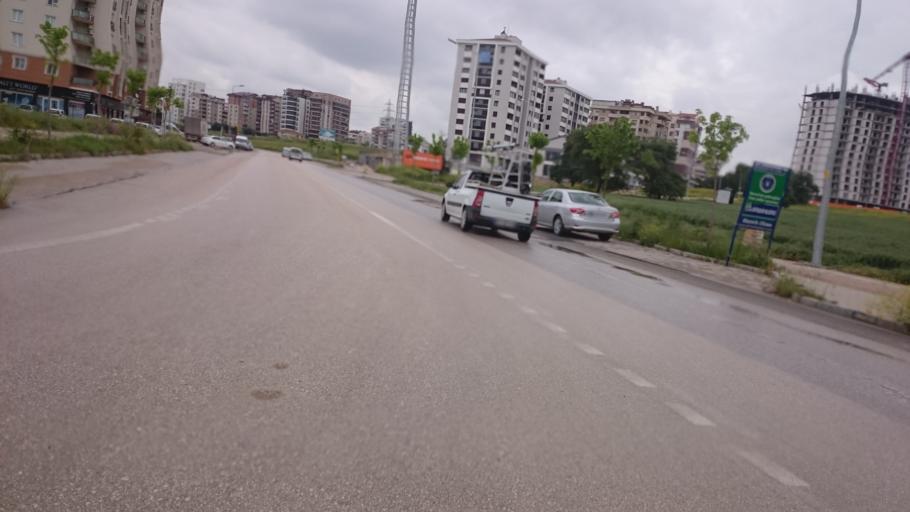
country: TR
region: Bursa
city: Cali
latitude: 40.2151
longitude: 28.9438
